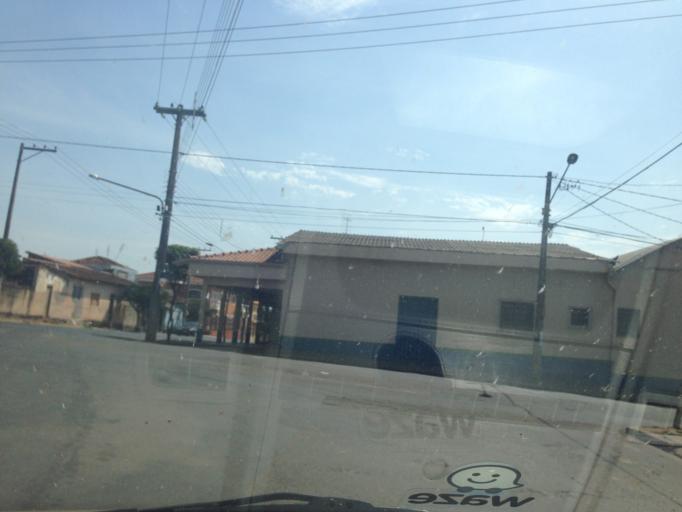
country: BR
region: Sao Paulo
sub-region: Casa Branca
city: Casa Branca
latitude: -21.7772
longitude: -47.0757
